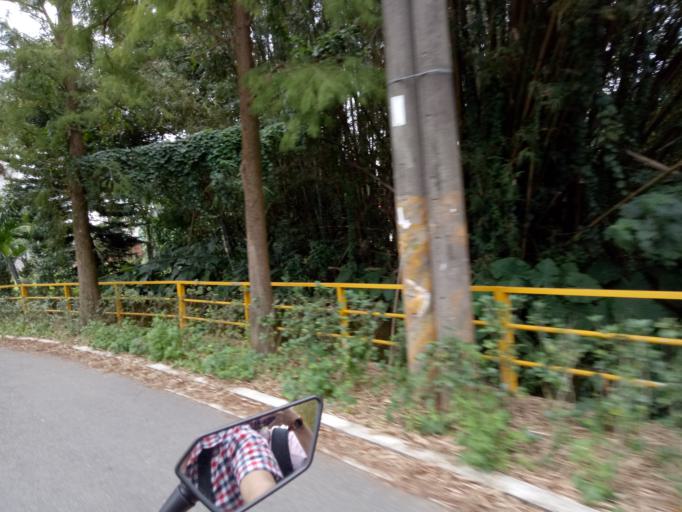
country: TW
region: Taiwan
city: Daxi
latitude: 24.8733
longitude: 121.2560
